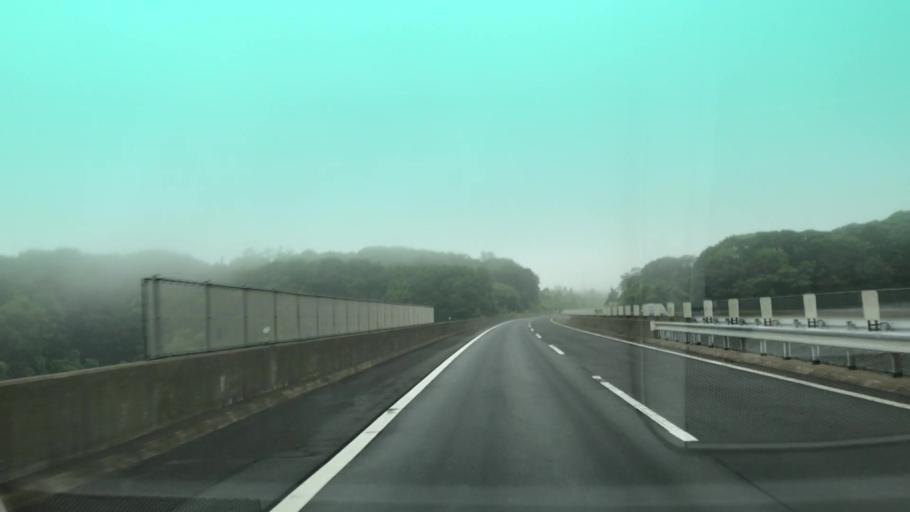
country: JP
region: Hokkaido
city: Shiraoi
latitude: 42.4503
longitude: 141.1595
